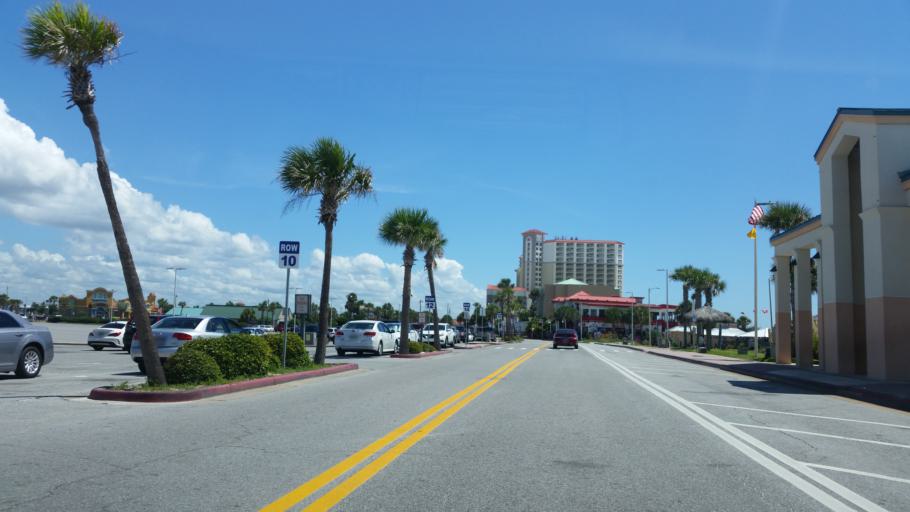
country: US
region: Florida
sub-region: Santa Rosa County
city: Gulf Breeze
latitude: 30.3318
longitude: -87.1413
